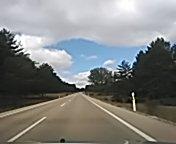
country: ES
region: Castille and Leon
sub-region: Provincia de Soria
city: San Leonardo de Yague
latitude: 41.8387
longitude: -3.0912
